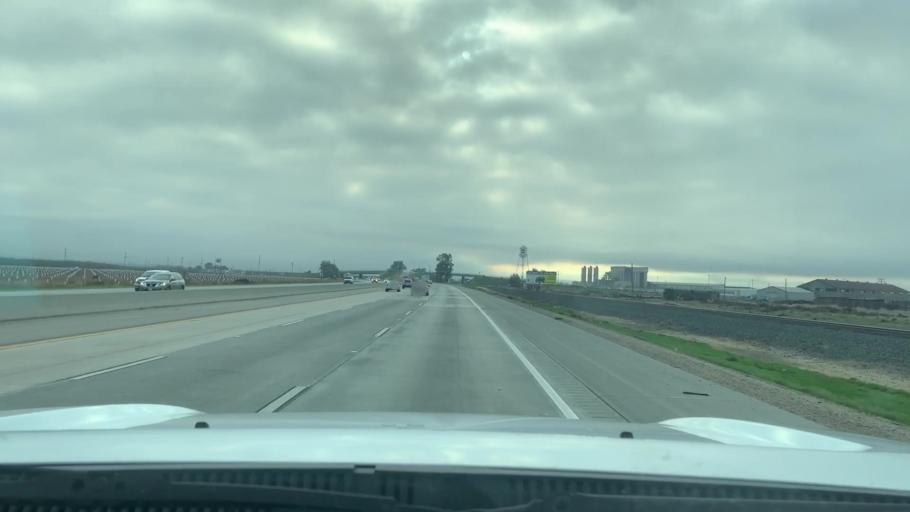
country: US
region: California
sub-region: Kern County
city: Shafter
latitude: 35.5047
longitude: -119.1712
